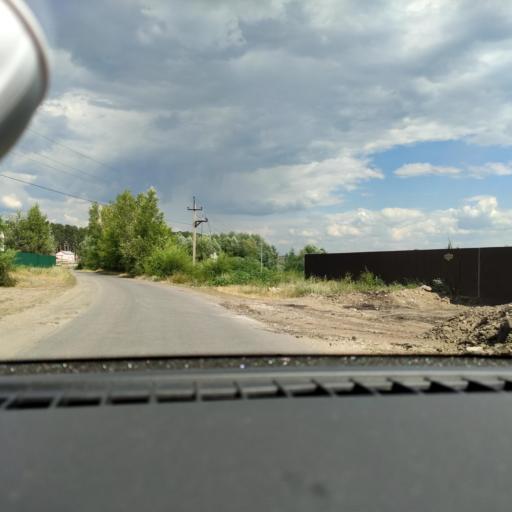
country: RU
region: Samara
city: Volzhskiy
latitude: 53.4290
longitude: 50.1363
